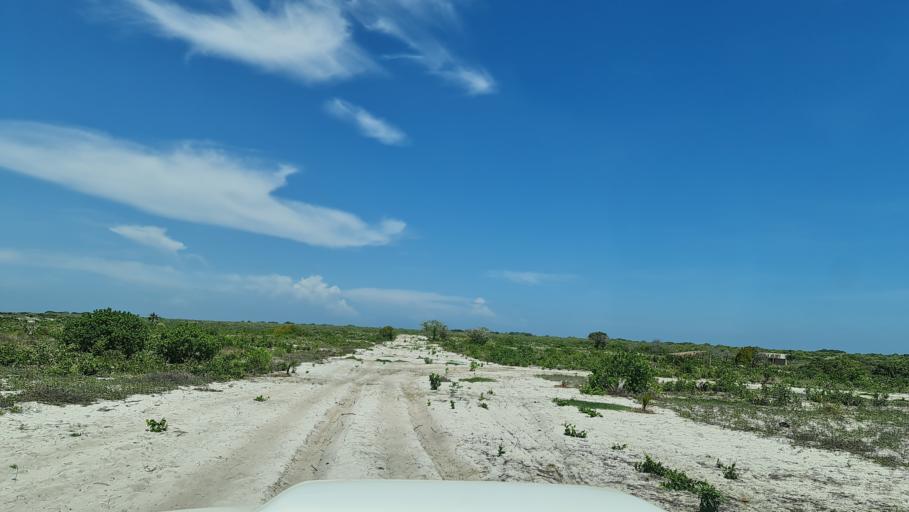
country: MZ
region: Nampula
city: Ilha de Mocambique
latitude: -15.1947
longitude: 40.6205
